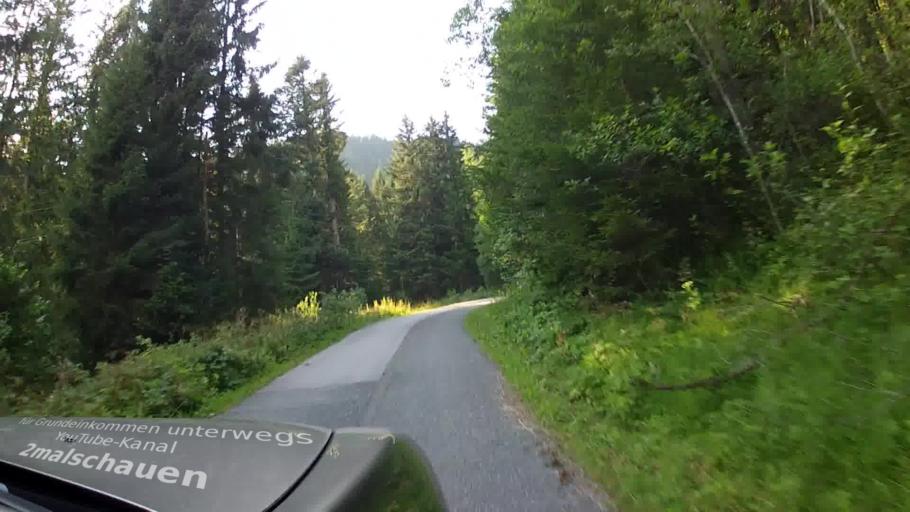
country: AT
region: Salzburg
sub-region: Politischer Bezirk Sankt Johann im Pongau
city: Eben im Pongau
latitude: 47.4327
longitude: 13.3808
